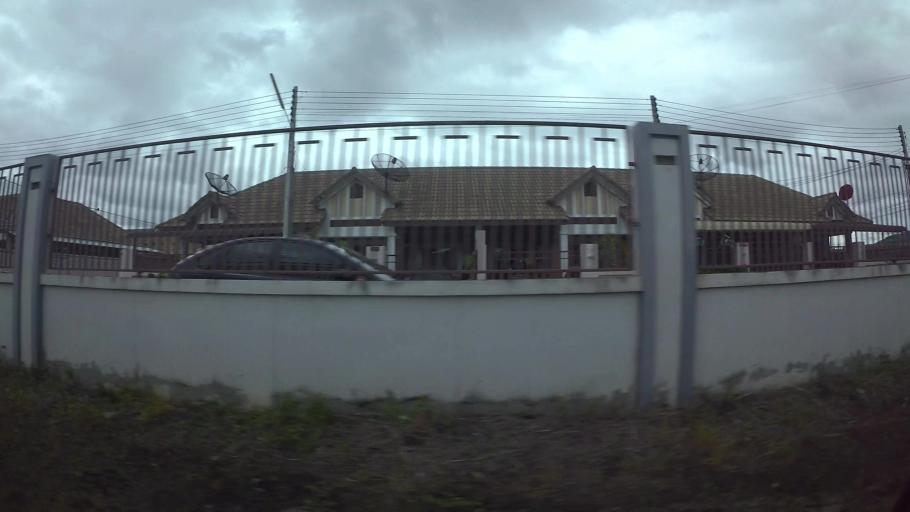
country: TH
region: Chon Buri
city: Sattahip
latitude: 12.7269
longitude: 100.8955
